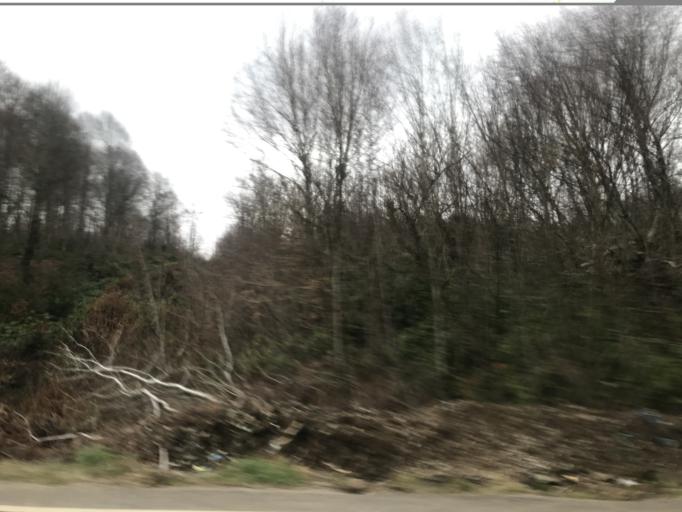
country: TR
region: Bartin
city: Amasra
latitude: 41.7155
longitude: 32.3941
